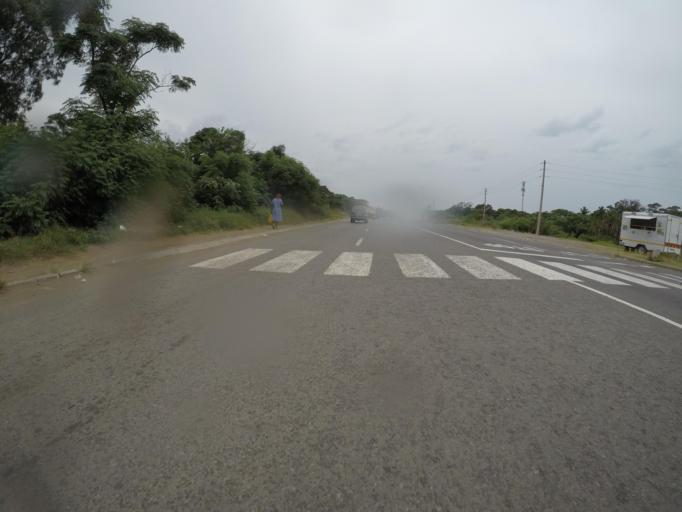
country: ZA
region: Eastern Cape
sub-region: Buffalo City Metropolitan Municipality
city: East London
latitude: -33.0000
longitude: 27.8419
